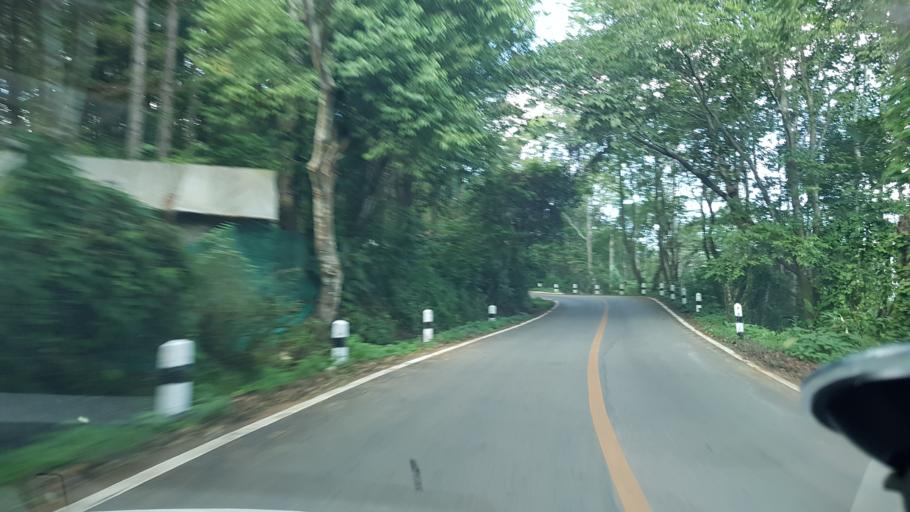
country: TH
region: Chiang Rai
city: Mae Fa Luang
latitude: 20.3321
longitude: 99.8141
